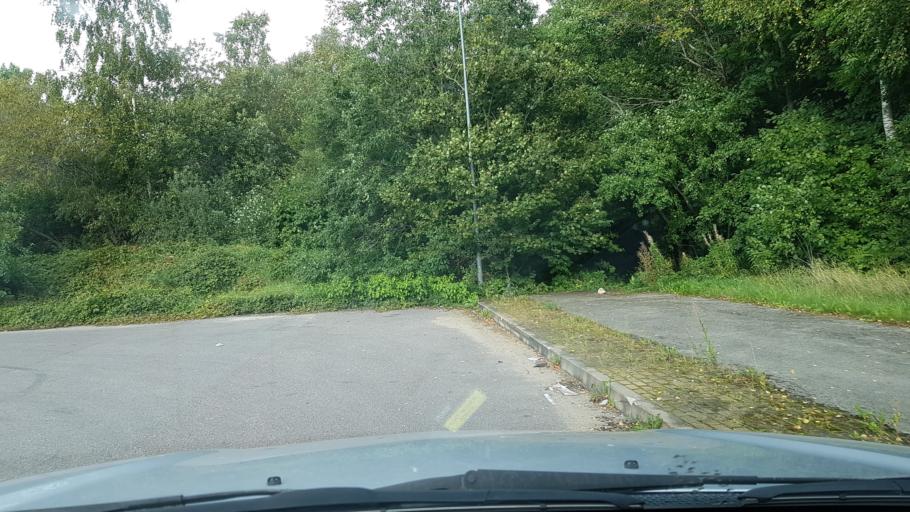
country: EE
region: Harju
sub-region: Rae vald
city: Jueri
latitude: 59.3717
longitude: 24.8792
